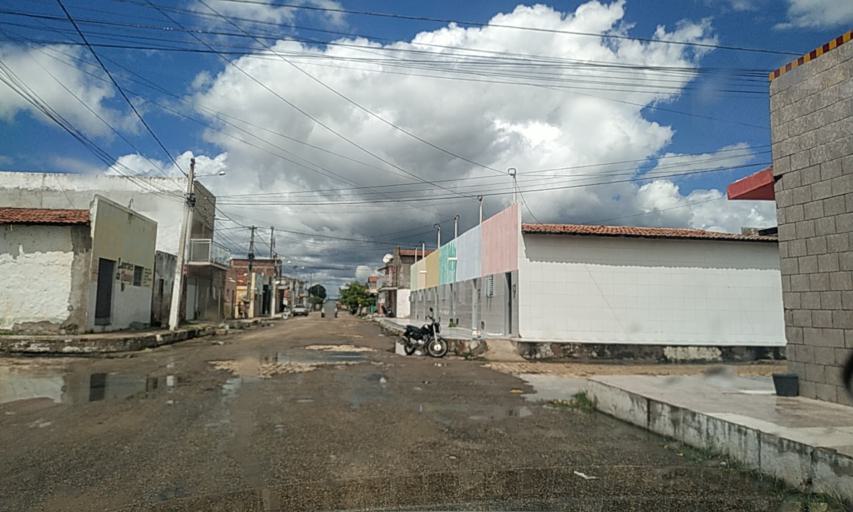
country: BR
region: Rio Grande do Norte
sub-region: Areia Branca
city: Areia Branca
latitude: -4.9521
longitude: -37.1322
